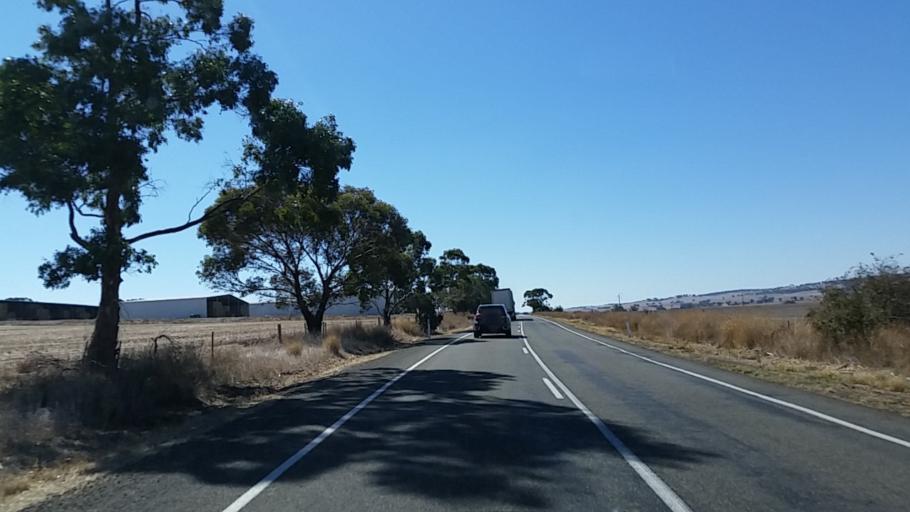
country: AU
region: South Australia
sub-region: Clare and Gilbert Valleys
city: Clare
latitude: -34.0264
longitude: 138.8041
